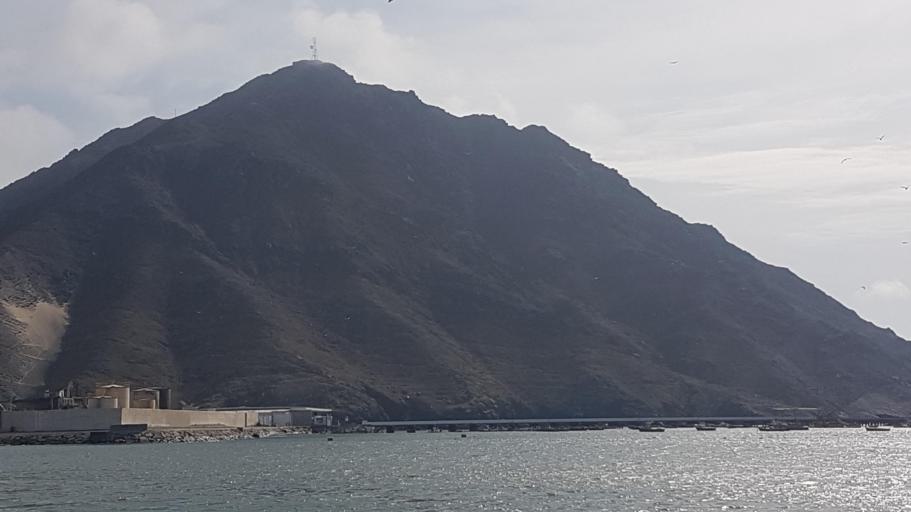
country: PE
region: Ancash
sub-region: Provincia de Santa
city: Samanco
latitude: -9.2527
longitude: -78.4949
